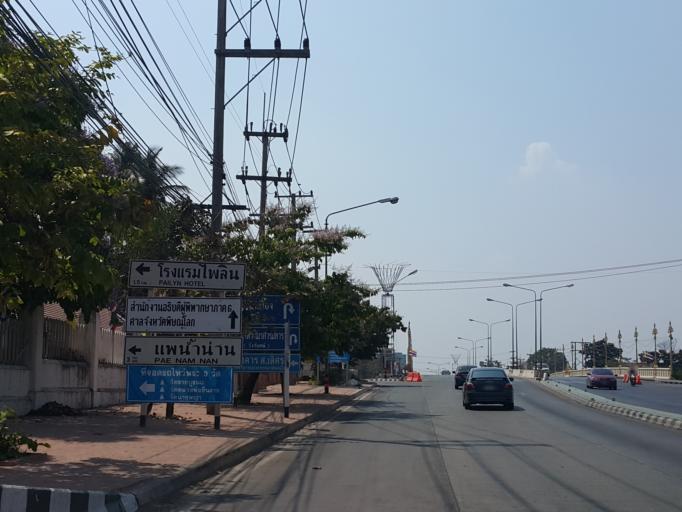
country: TH
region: Phitsanulok
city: Phitsanulok
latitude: 16.8219
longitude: 100.2615
